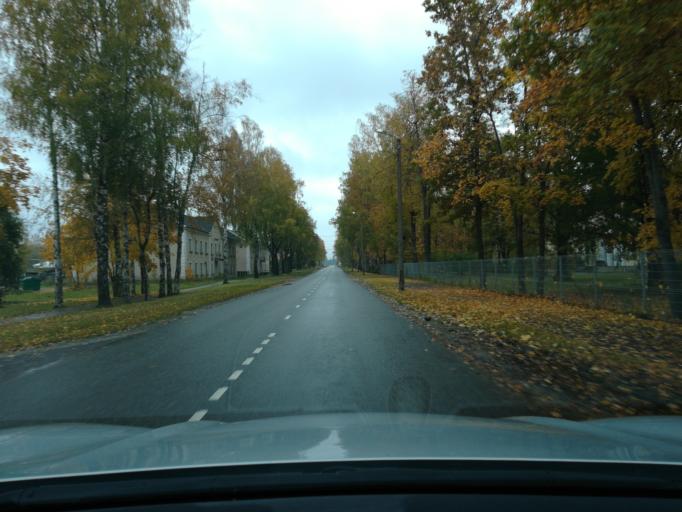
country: EE
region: Ida-Virumaa
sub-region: Johvi vald
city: Johvi
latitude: 59.3111
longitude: 27.4537
